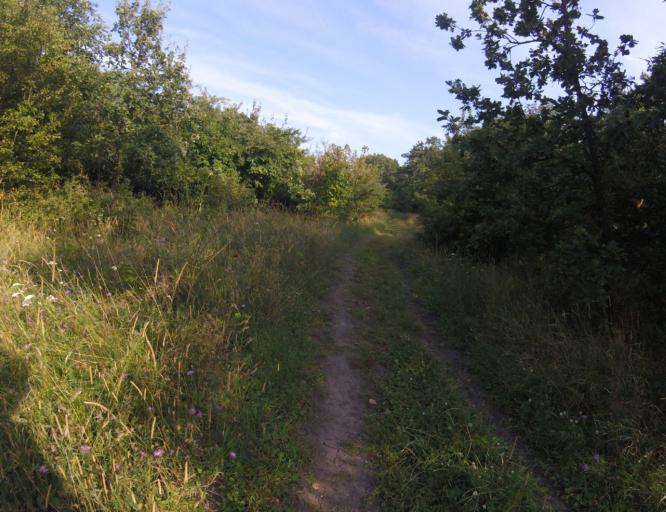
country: HU
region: Pest
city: Nagykovacsi
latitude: 47.6777
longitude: 19.0111
